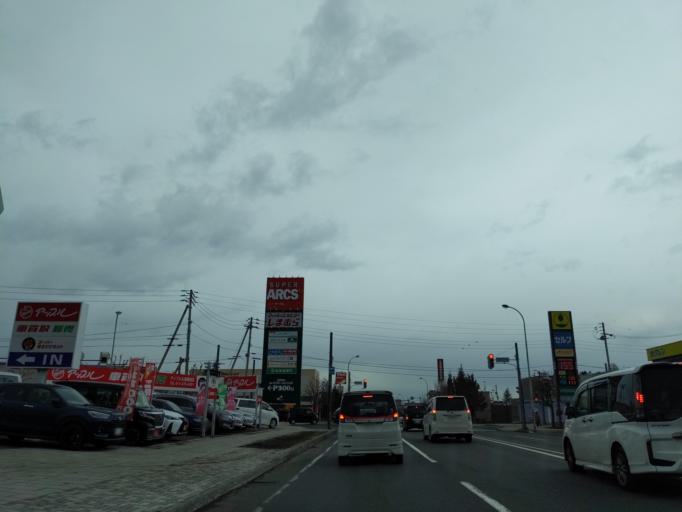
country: JP
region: Hokkaido
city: Sapporo
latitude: 43.1418
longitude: 141.3714
